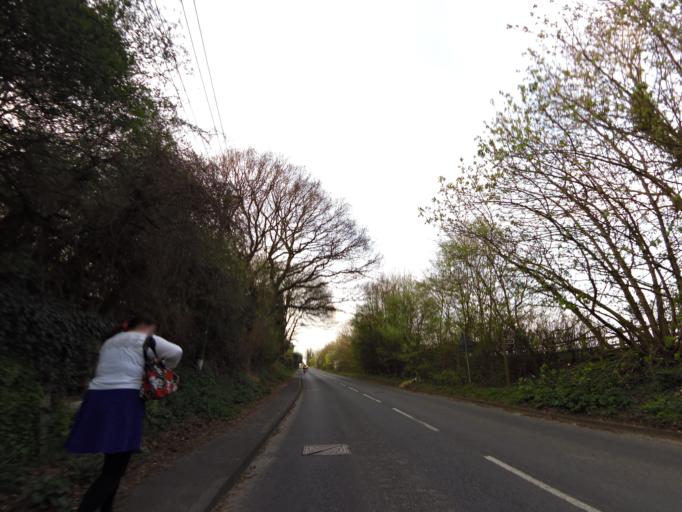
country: GB
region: England
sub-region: Suffolk
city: Ipswich
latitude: 52.1085
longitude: 1.1896
